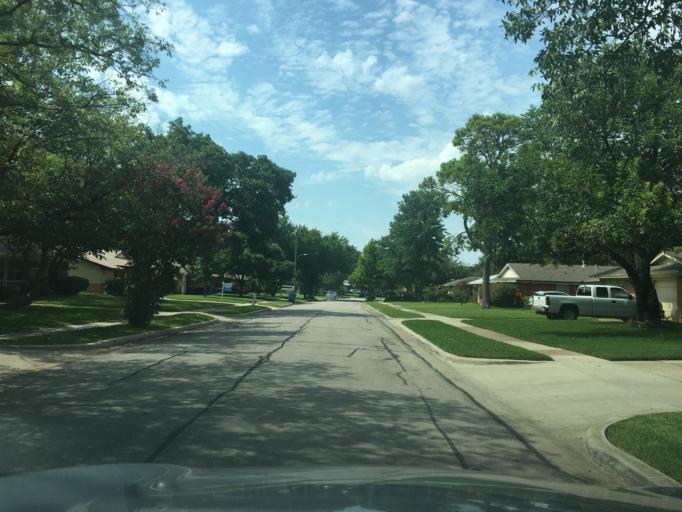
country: US
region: Texas
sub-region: Dallas County
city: Farmers Branch
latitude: 32.9299
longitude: -96.8702
